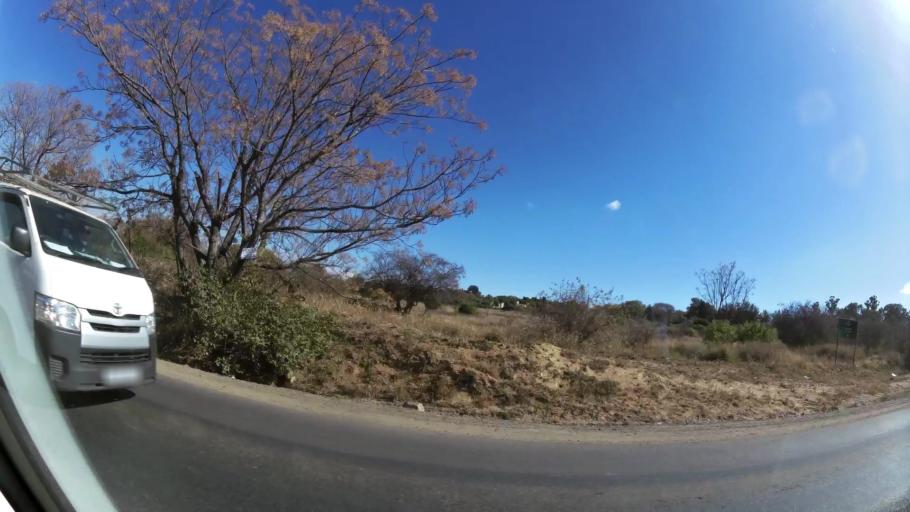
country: ZA
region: Gauteng
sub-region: City of Johannesburg Metropolitan Municipality
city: Midrand
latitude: -25.9737
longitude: 28.0790
